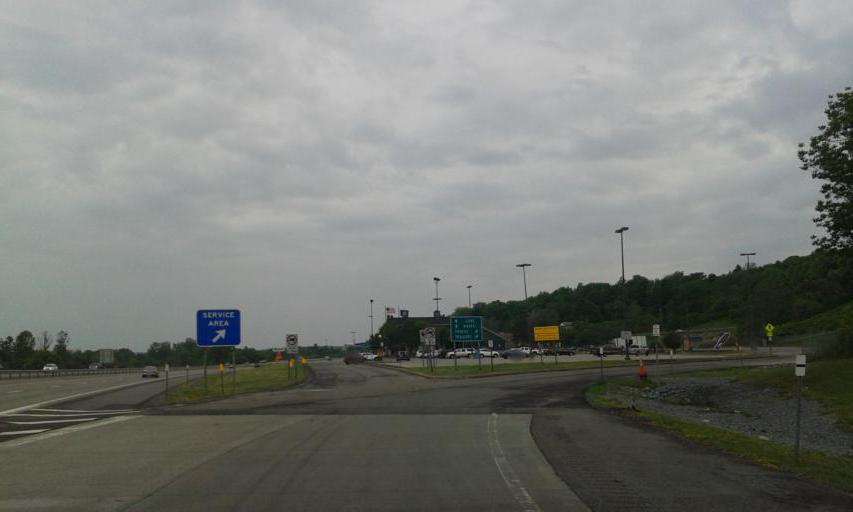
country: US
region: New York
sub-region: Onondaga County
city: Seneca Knolls
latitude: 43.0927
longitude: -76.3166
